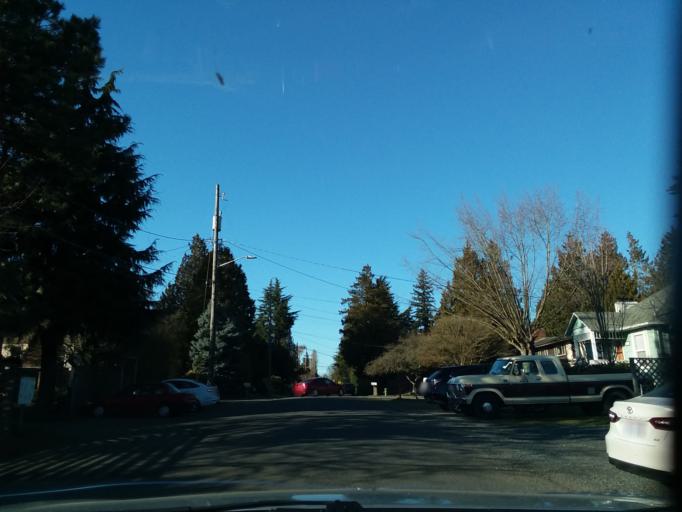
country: US
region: Washington
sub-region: King County
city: Shoreline
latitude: 47.7056
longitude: -122.3542
